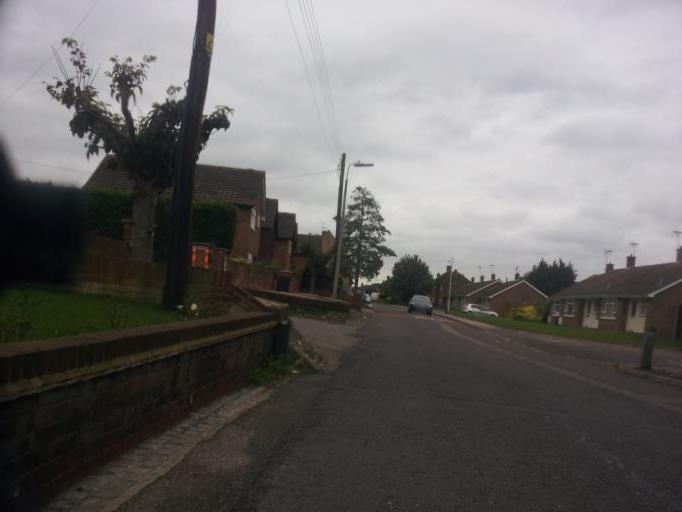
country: GB
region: England
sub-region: Kent
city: Teynham
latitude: 51.3295
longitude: 0.8041
